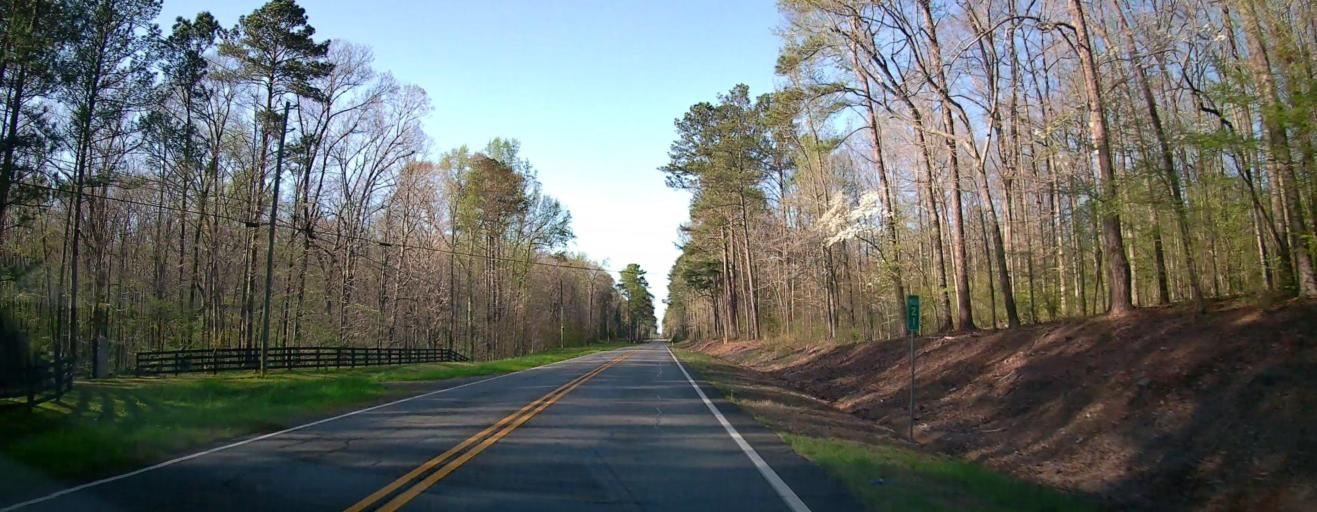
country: US
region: Georgia
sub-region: Monroe County
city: Forsyth
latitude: 33.1249
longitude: -83.9439
